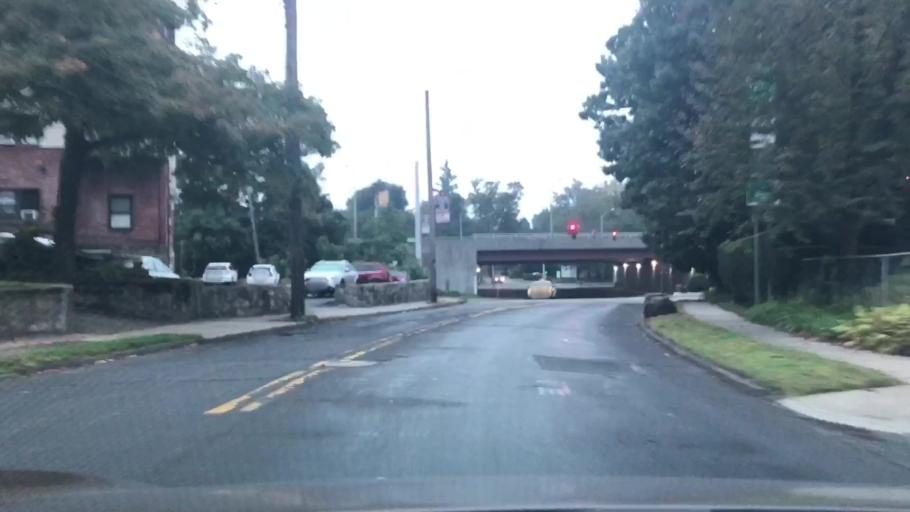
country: US
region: New York
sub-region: Westchester County
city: Bronxville
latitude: 40.9239
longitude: -73.8217
